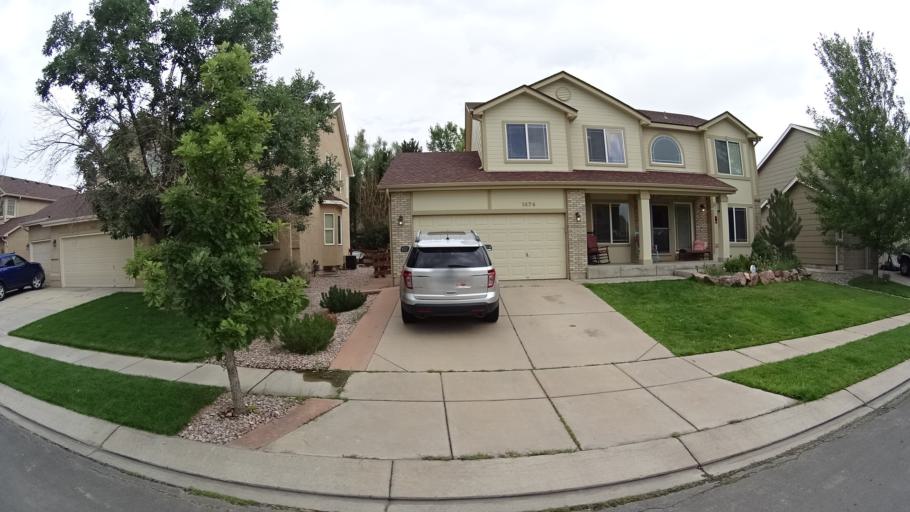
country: US
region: Colorado
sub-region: El Paso County
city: Gleneagle
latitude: 39.0059
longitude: -104.7998
